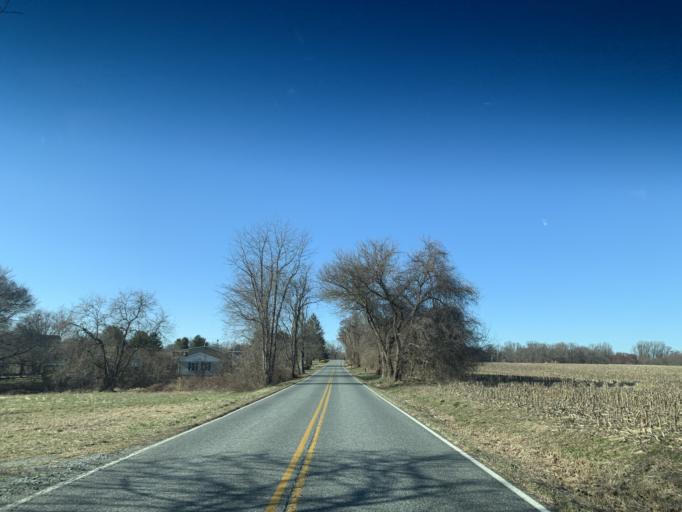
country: US
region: Maryland
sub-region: Cecil County
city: Rising Sun
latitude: 39.6369
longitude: -76.1053
